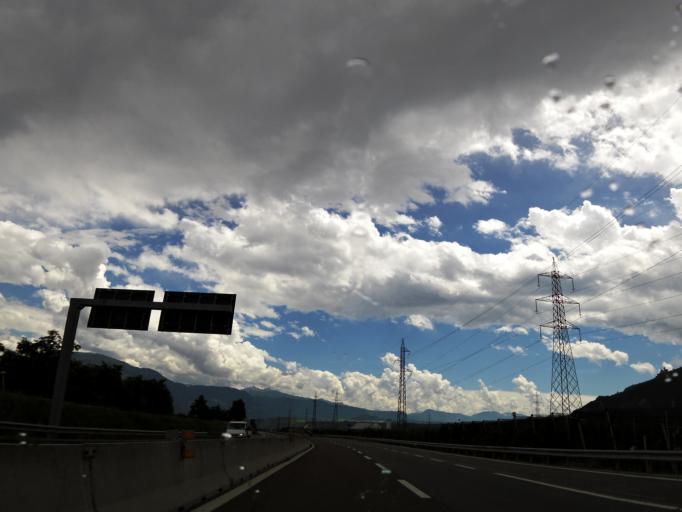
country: IT
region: Trentino-Alto Adige
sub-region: Bolzano
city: Terlano
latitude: 46.5202
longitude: 11.2460
